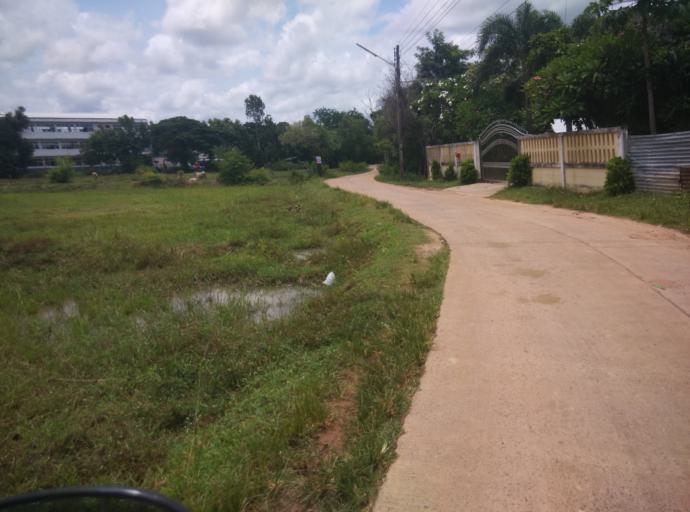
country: TH
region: Sisaket
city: Si Sa Ket
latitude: 15.1078
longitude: 104.3568
